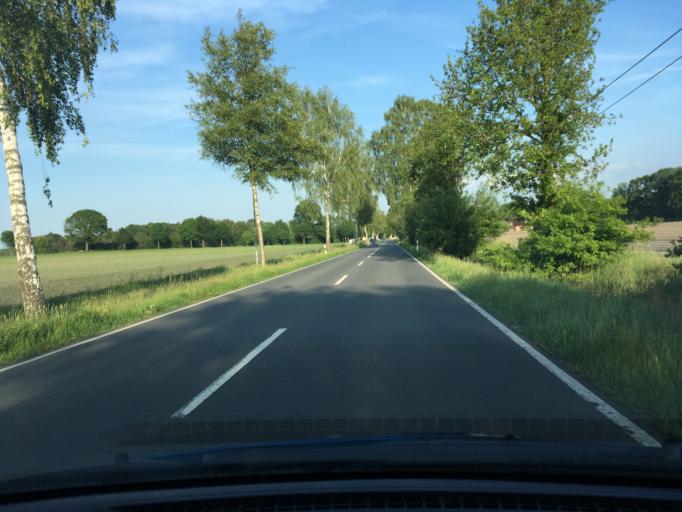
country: DE
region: Lower Saxony
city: Welle
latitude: 53.2483
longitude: 9.7796
